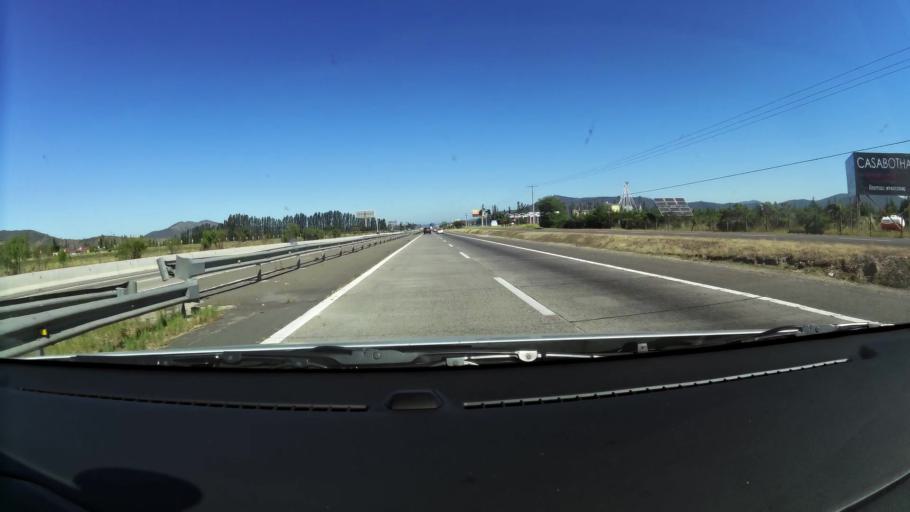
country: CL
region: Valparaiso
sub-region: Provincia de Marga Marga
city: Villa Alemana
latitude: -33.3546
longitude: -71.3350
